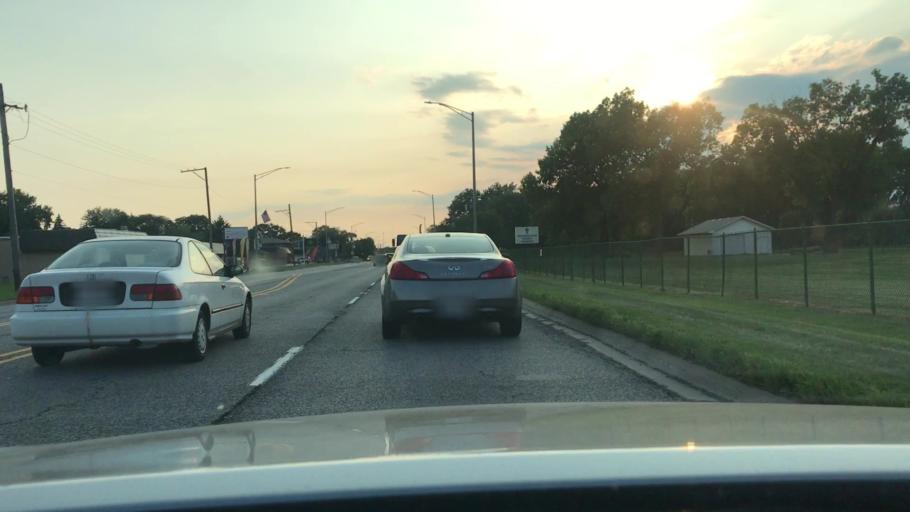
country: US
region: Illinois
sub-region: Cook County
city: Justice
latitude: 41.7475
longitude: -87.8303
